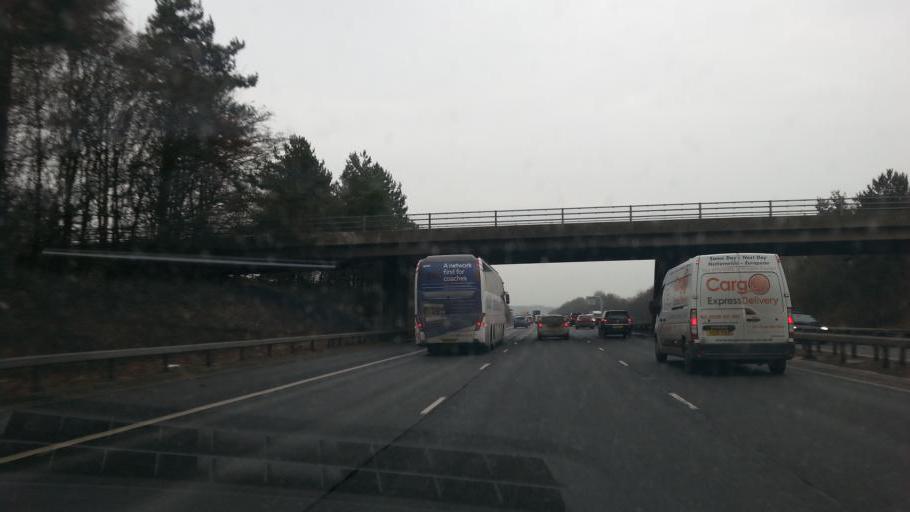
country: GB
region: England
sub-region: Hertfordshire
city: Sawbridgeworth
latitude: 51.7823
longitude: 0.1676
